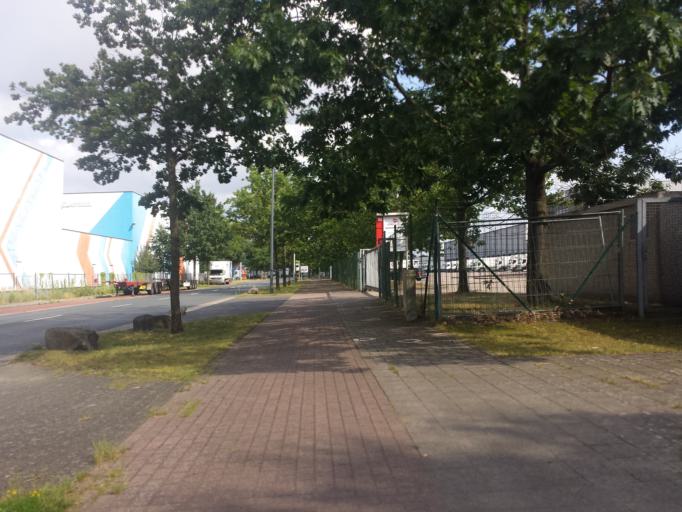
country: DE
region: Lower Saxony
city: Stuhr
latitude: 53.0883
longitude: 8.7094
